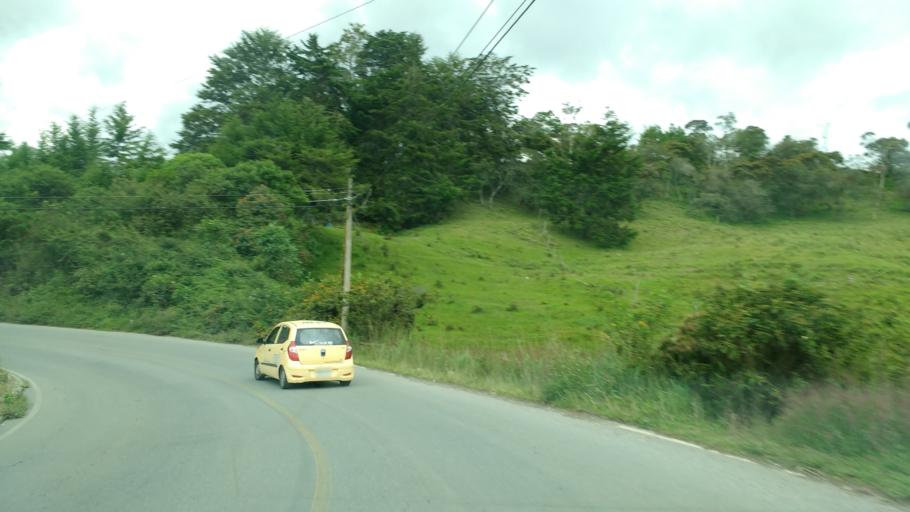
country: CO
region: Antioquia
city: Marinilla
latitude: 6.1843
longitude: -75.2960
